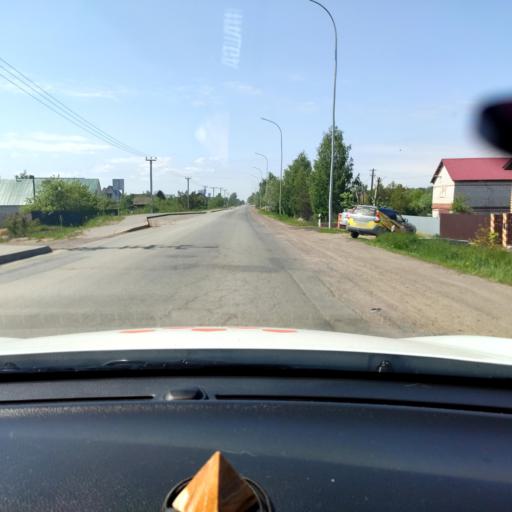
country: RU
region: Tatarstan
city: Stolbishchi
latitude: 55.6960
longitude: 49.1954
